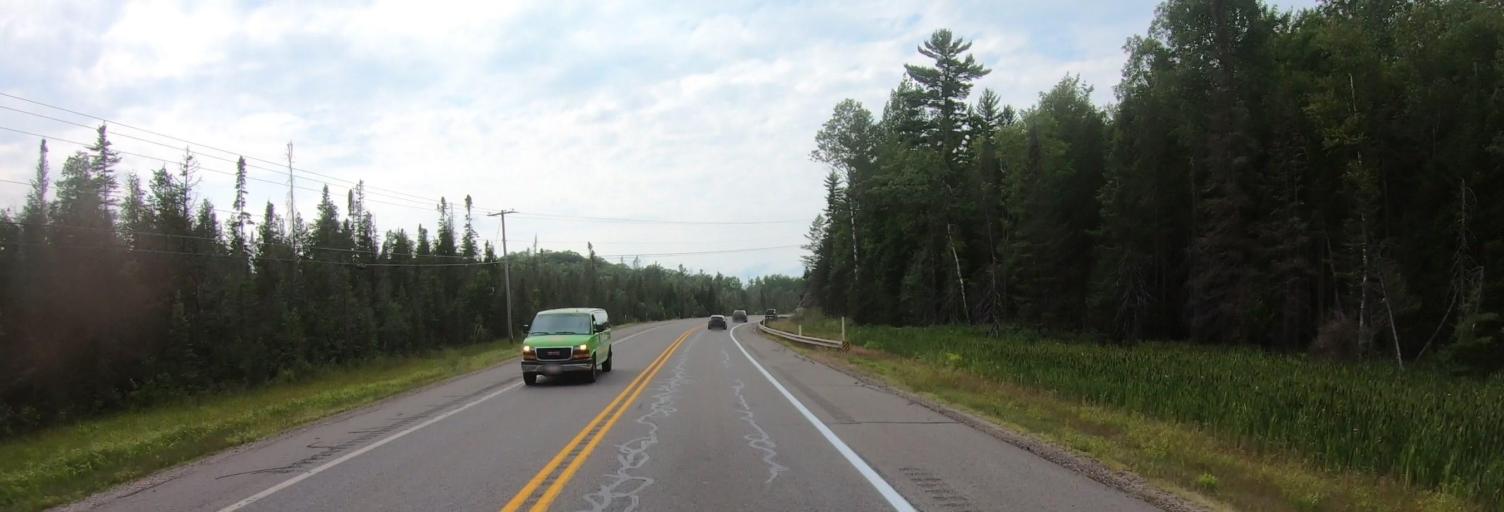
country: US
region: Michigan
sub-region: Marquette County
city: West Ishpeming
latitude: 46.5003
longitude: -87.9486
